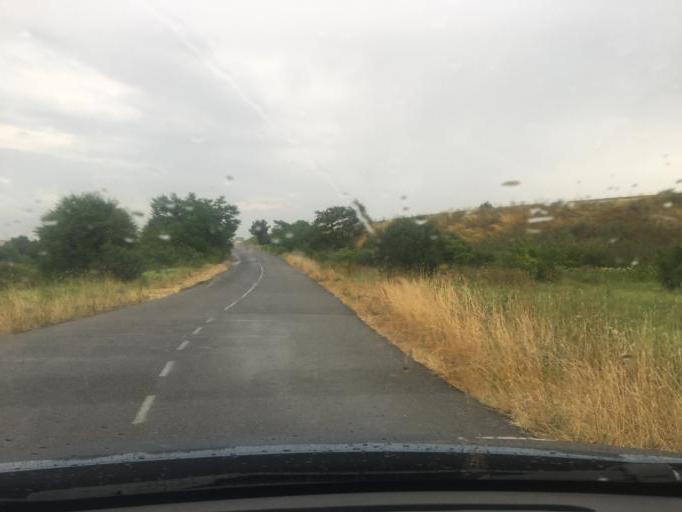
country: BG
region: Burgas
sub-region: Obshtina Burgas
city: Burgas
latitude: 42.5508
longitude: 27.4898
